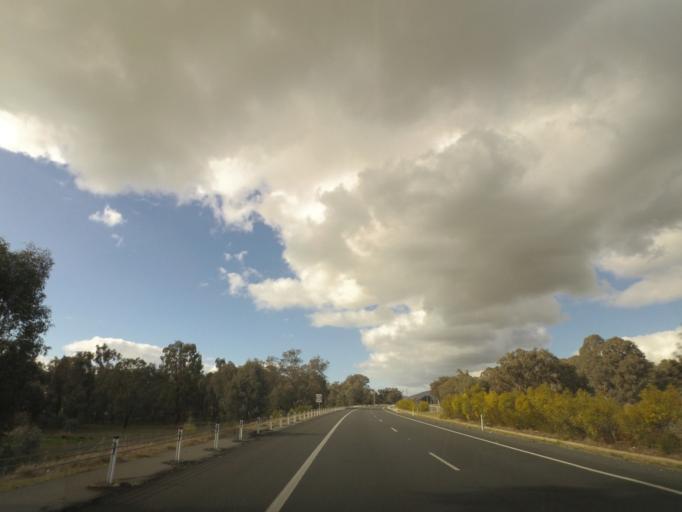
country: AU
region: New South Wales
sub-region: Greater Hume Shire
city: Holbrook
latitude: -35.7064
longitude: 147.3113
